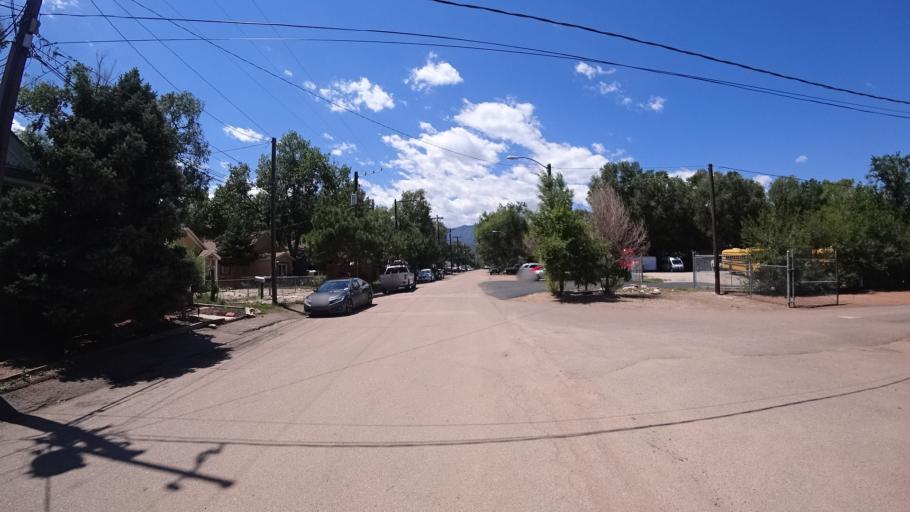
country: US
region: Colorado
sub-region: El Paso County
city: Colorado Springs
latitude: 38.8129
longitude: -104.8160
